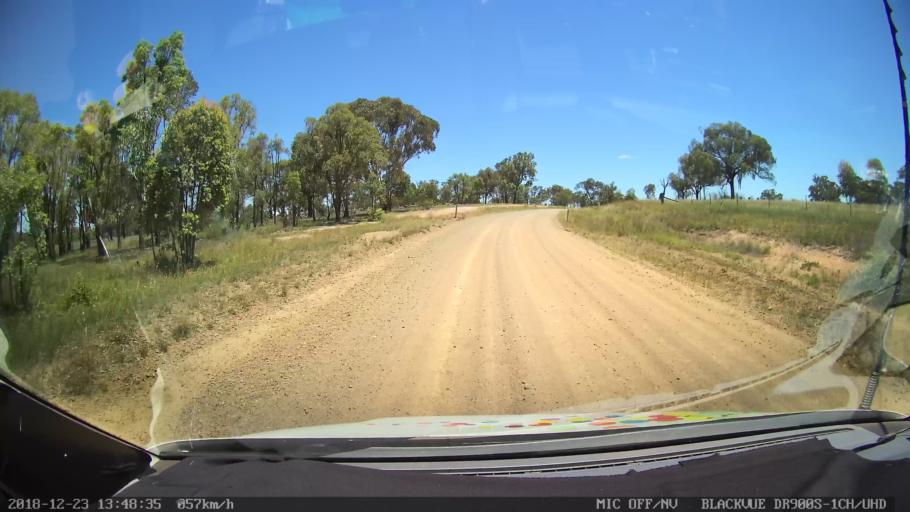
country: AU
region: New South Wales
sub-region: Tamworth Municipality
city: Manilla
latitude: -30.5186
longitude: 151.1157
